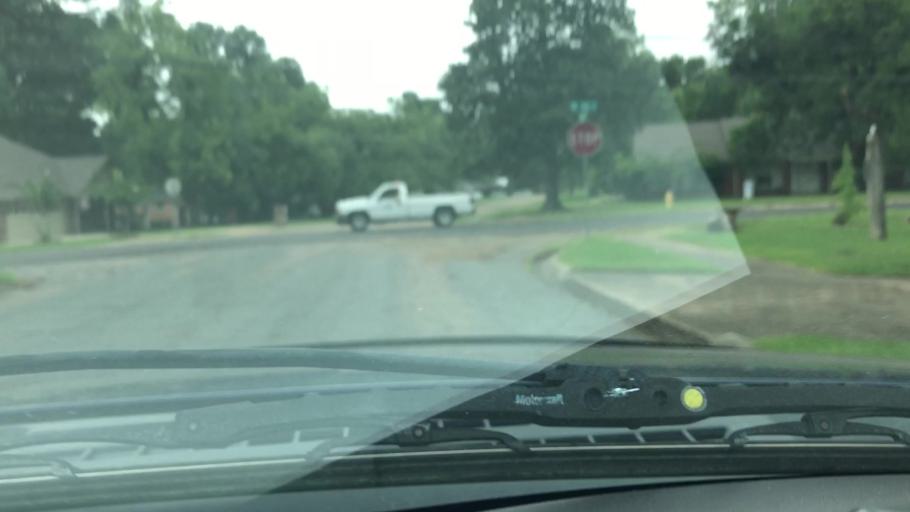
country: US
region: Arkansas
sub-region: Miller County
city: Texarkana
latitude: 33.4560
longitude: -94.0570
